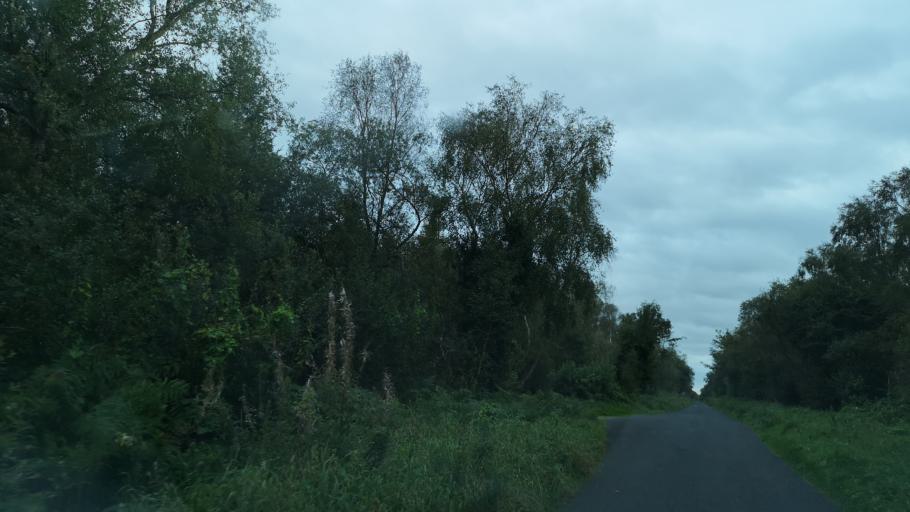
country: IE
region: Leinster
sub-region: Uibh Fhaili
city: Ferbane
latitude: 53.1985
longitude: -7.7253
